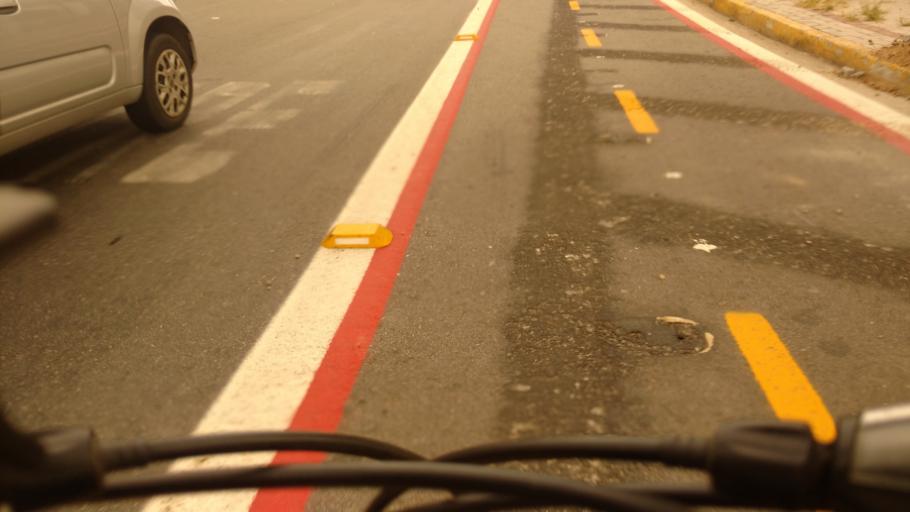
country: BR
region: Ceara
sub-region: Fortaleza
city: Fortaleza
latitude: -3.7474
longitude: -38.4895
